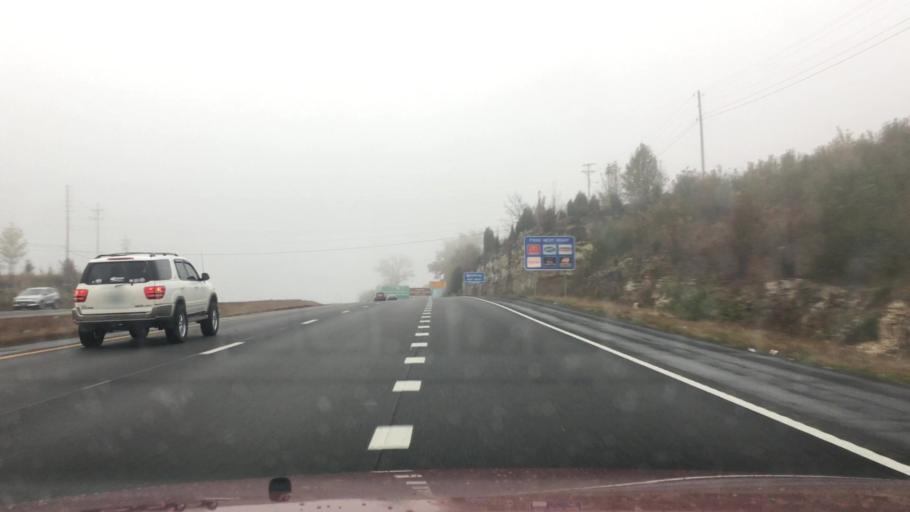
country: US
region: Missouri
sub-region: Taney County
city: Branson
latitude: 36.6646
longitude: -93.2219
